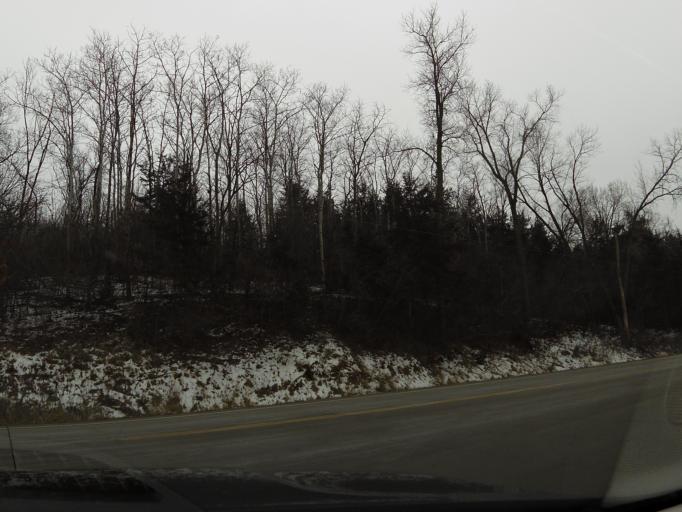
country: US
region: Minnesota
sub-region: Scott County
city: Jordan
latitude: 44.6534
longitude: -93.6363
